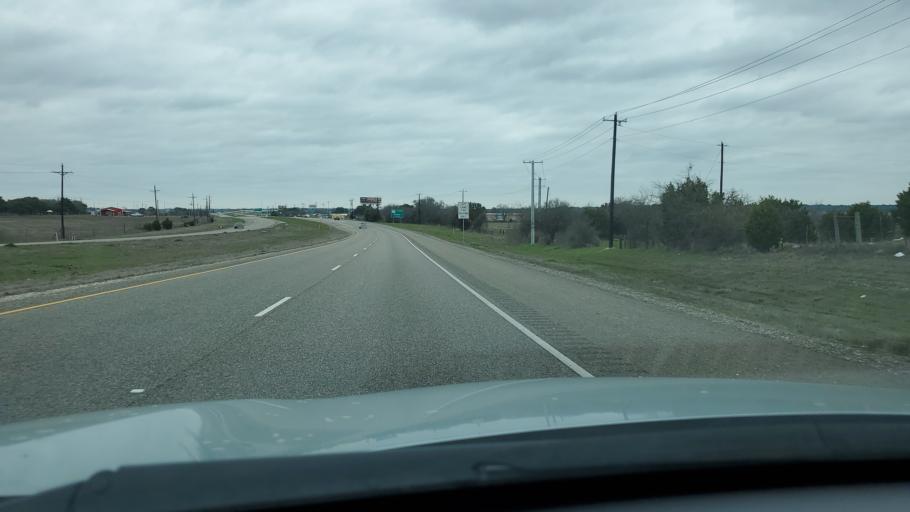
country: US
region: Texas
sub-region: Williamson County
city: Florence
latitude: 30.8102
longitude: -97.7723
